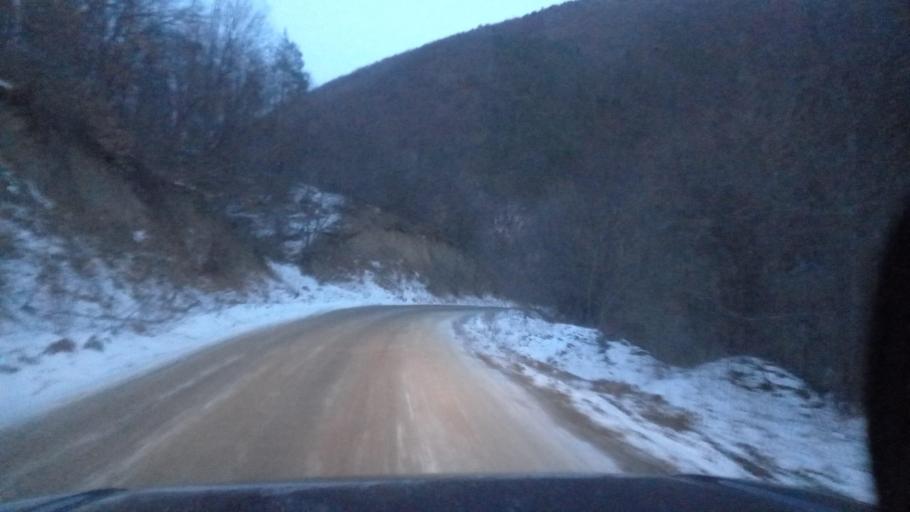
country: RU
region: Ingushetiya
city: Dzhayrakh
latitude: 42.8287
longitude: 44.6145
